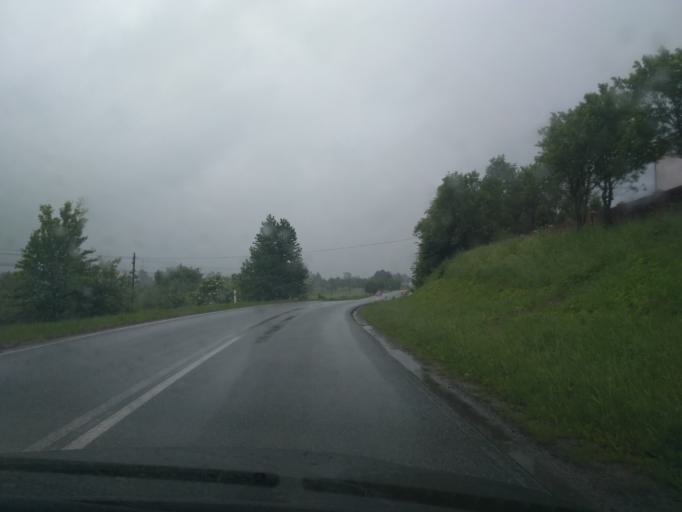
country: PL
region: Subcarpathian Voivodeship
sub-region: Powiat krosnienski
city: Leki
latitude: 49.7973
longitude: 21.6489
